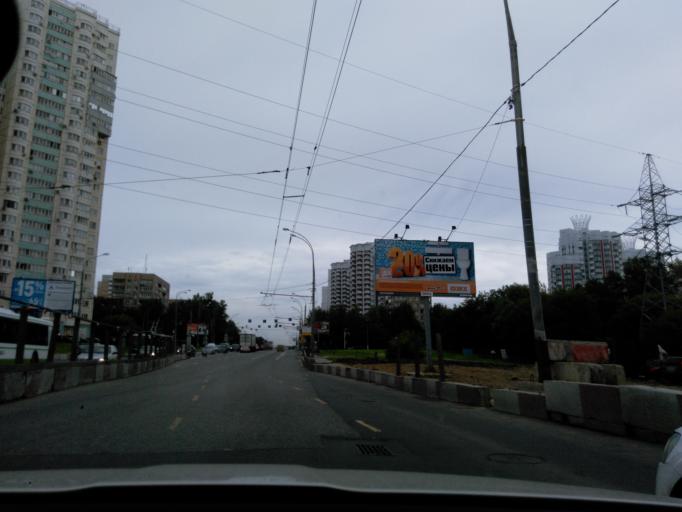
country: RU
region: Moscow
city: Tsaritsyno
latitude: 55.6424
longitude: 37.6559
